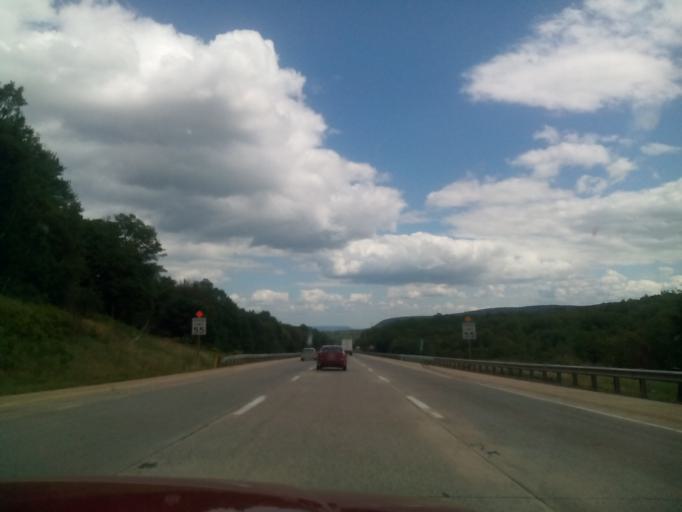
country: US
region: Pennsylvania
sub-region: Monroe County
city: Emerald Lakes
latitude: 41.0668
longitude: -75.3869
